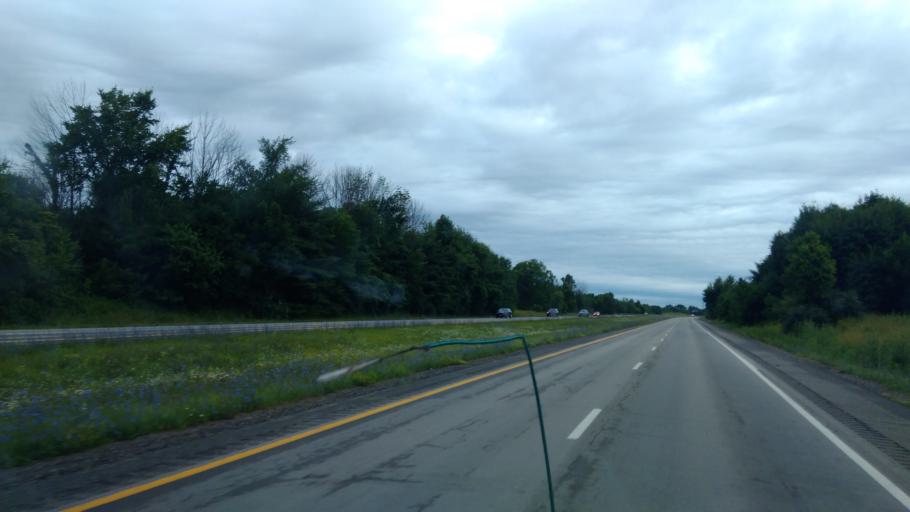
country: US
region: Ohio
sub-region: Columbiana County
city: Lisbon
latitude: 40.8175
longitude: -80.7452
